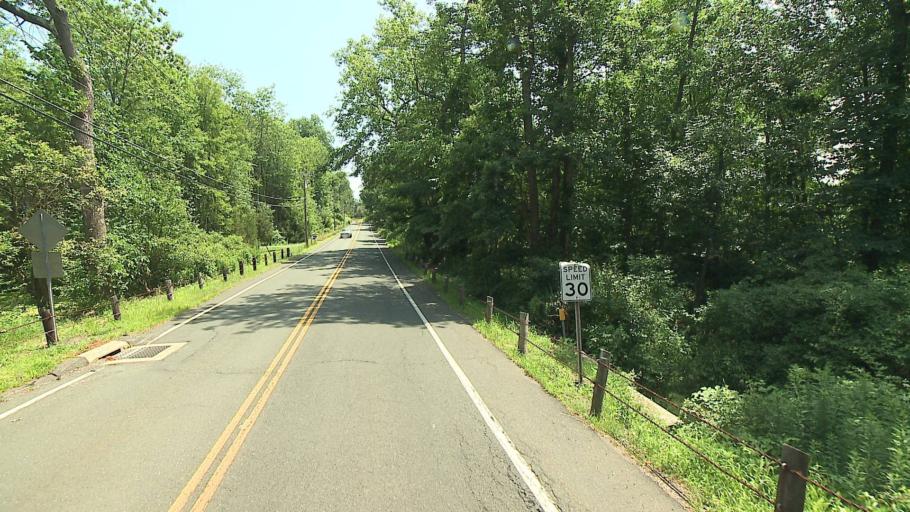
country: US
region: Connecticut
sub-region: Hartford County
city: Tariffville
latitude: 41.9186
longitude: -72.7470
